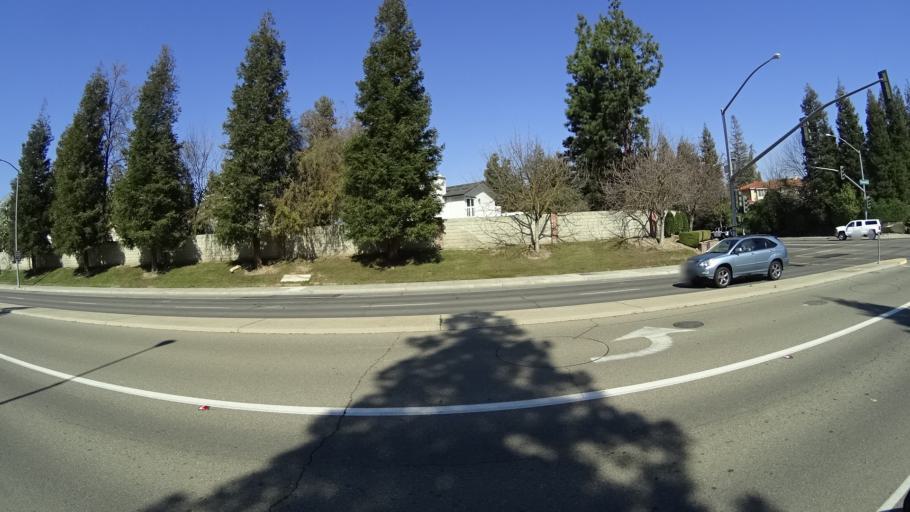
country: US
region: California
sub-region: Fresno County
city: Clovis
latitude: 36.8772
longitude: -119.7711
